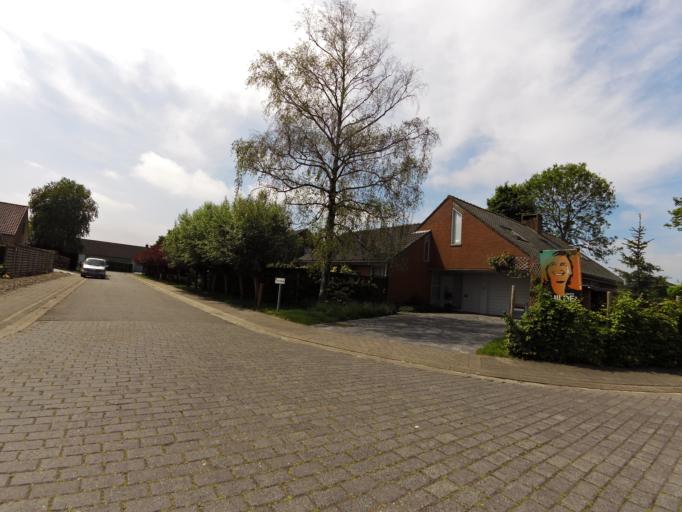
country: BE
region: Flanders
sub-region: Provincie West-Vlaanderen
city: Ichtegem
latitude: 51.0983
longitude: 3.0114
